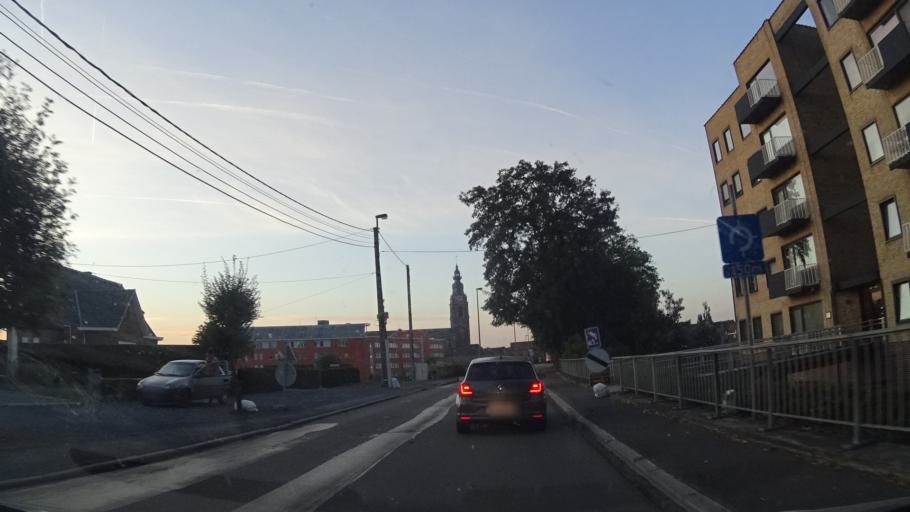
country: BE
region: Wallonia
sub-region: Province du Hainaut
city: Frasnes-lez-Buissenal
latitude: 50.6029
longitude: 3.6202
